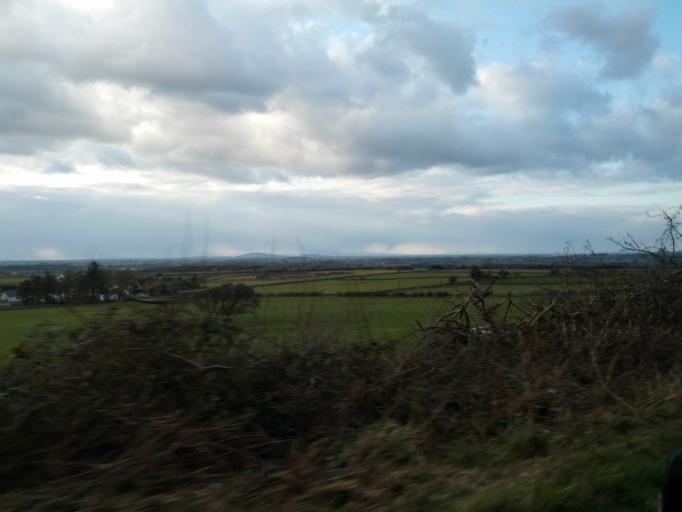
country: IE
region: Connaught
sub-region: County Galway
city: Athenry
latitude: 53.4130
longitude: -8.7518
